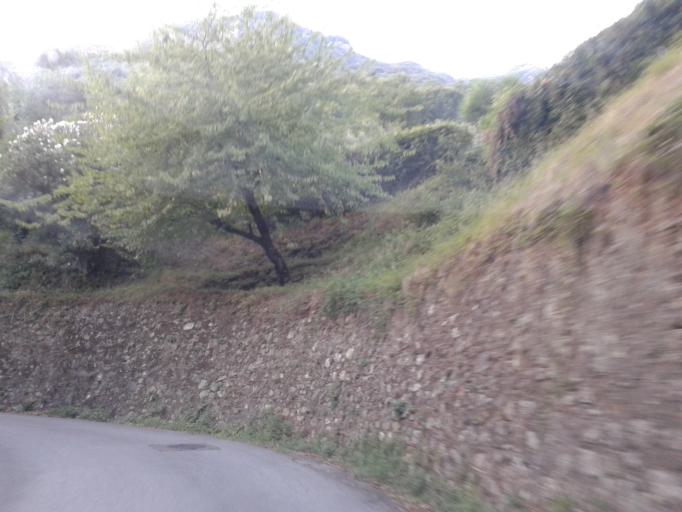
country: IT
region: Tuscany
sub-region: Provincia di Lucca
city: Corsanico-Bargecchia
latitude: 43.9542
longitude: 10.3206
